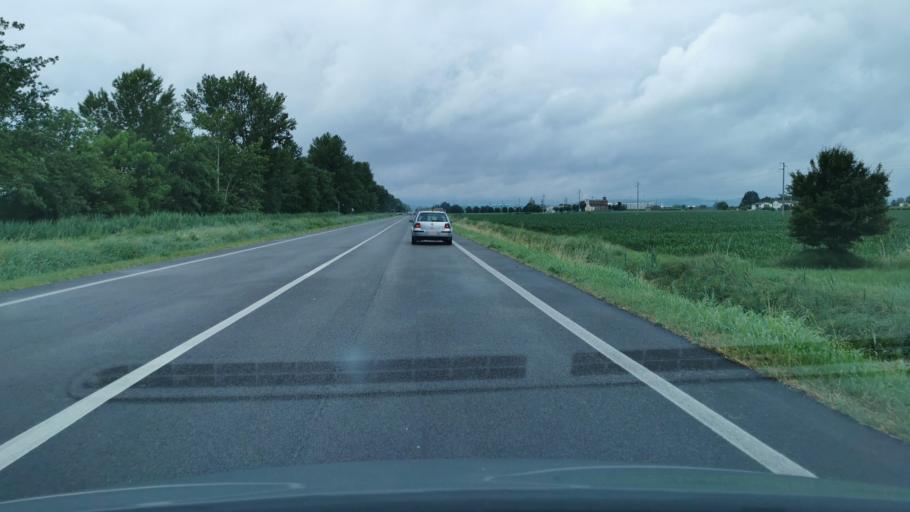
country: IT
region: Emilia-Romagna
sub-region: Provincia di Ravenna
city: Granarolo
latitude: 44.3424
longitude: 11.9211
